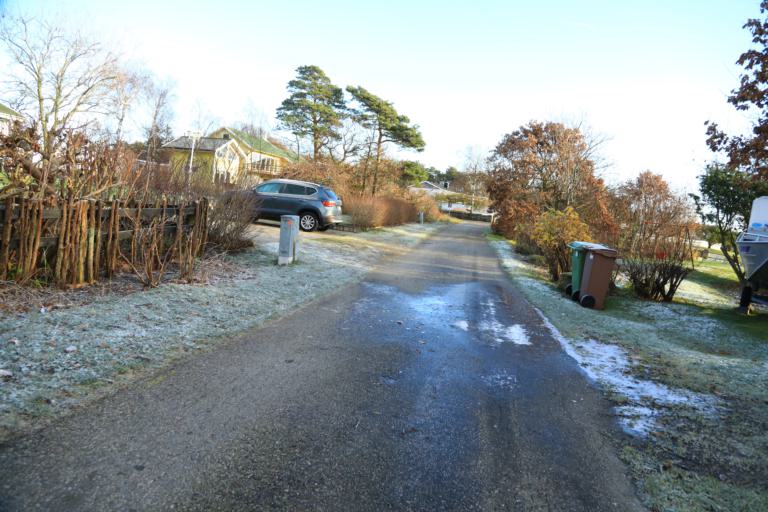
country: SE
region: Halland
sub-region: Varbergs Kommun
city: Varberg
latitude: 57.1891
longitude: 12.1945
